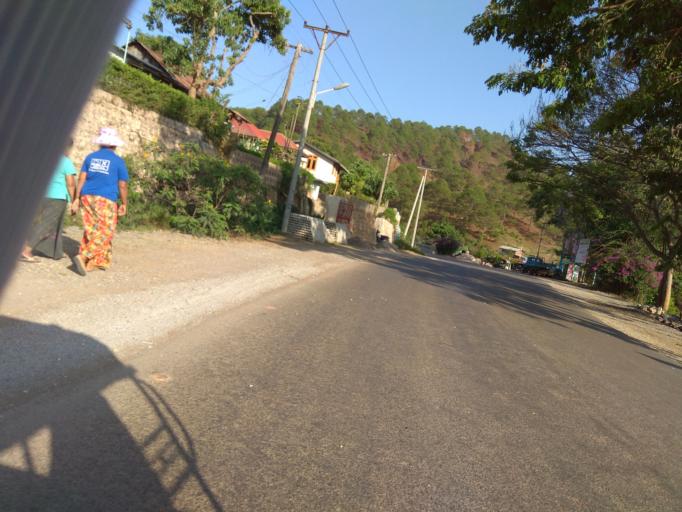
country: MM
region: Mandalay
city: Yamethin
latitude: 20.6329
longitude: 96.5770
